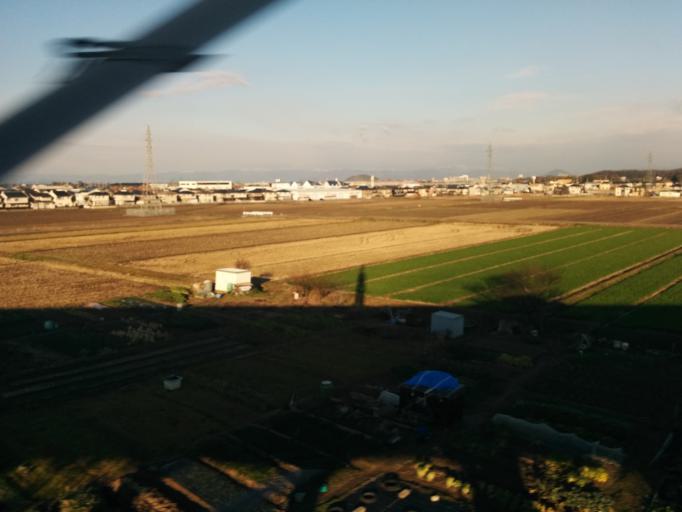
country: JP
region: Shiga Prefecture
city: Nagahama
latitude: 35.3410
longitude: 136.2999
